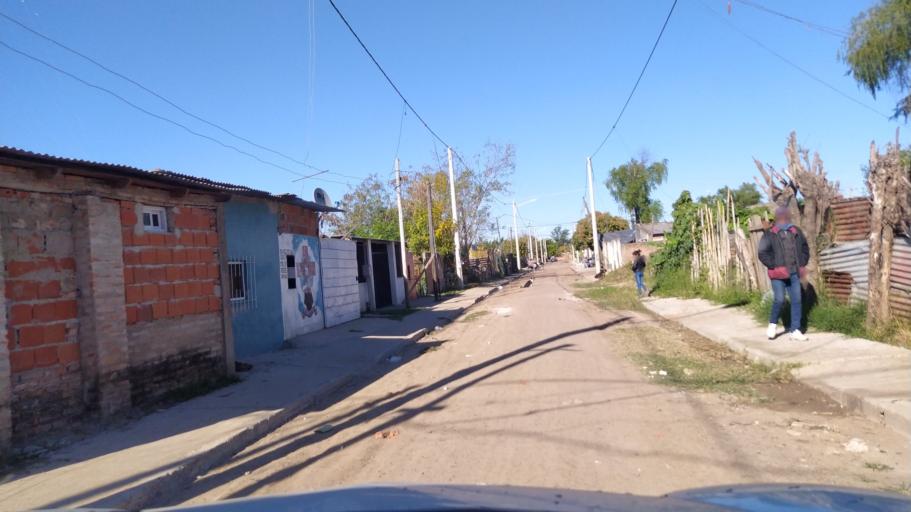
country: AR
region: Corrientes
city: Corrientes
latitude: -27.4951
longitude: -58.8064
